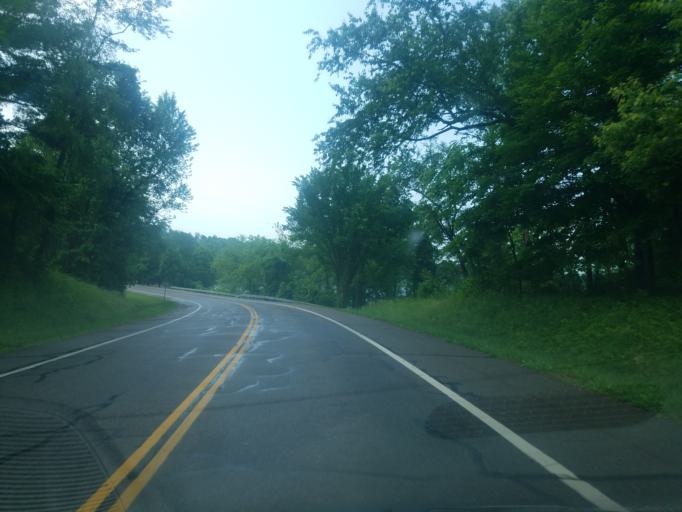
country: US
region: Ohio
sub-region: Tuscarawas County
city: Rockford
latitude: 40.5444
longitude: -81.2465
